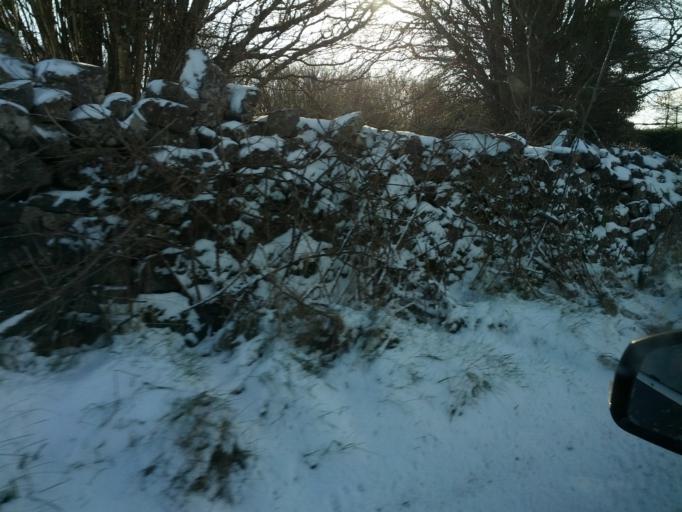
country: IE
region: Connaught
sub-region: County Galway
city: Oranmore
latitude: 53.2021
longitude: -8.8528
